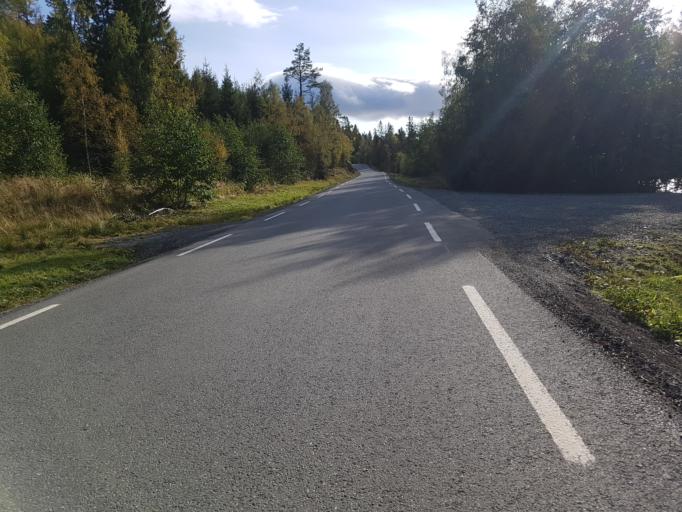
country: NO
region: Sor-Trondelag
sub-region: Malvik
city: Malvik
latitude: 63.3555
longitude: 10.6395
